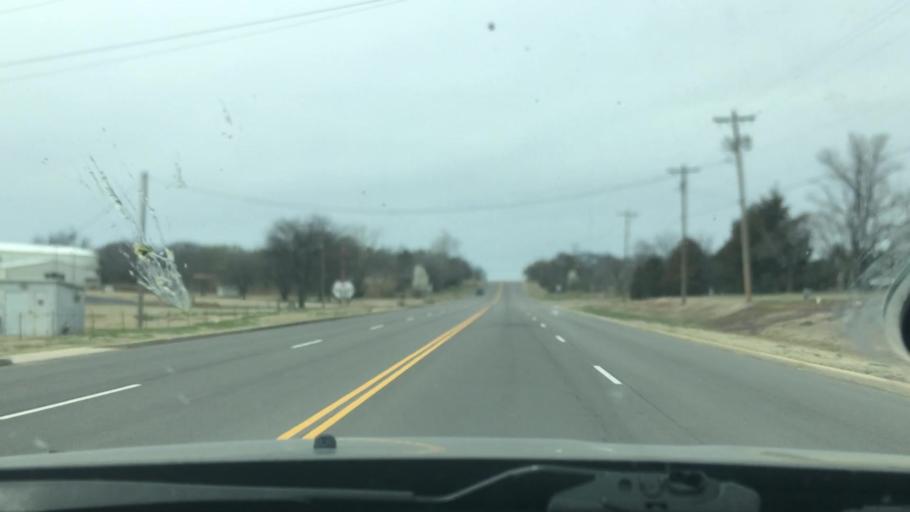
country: US
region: Oklahoma
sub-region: Seminole County
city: Seminole
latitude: 35.2525
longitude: -96.7056
